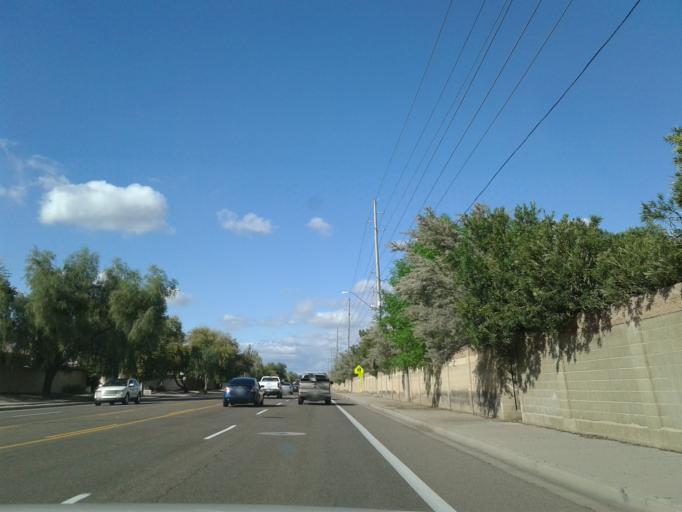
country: US
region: Arizona
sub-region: Maricopa County
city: Paradise Valley
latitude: 33.6449
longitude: -111.9600
